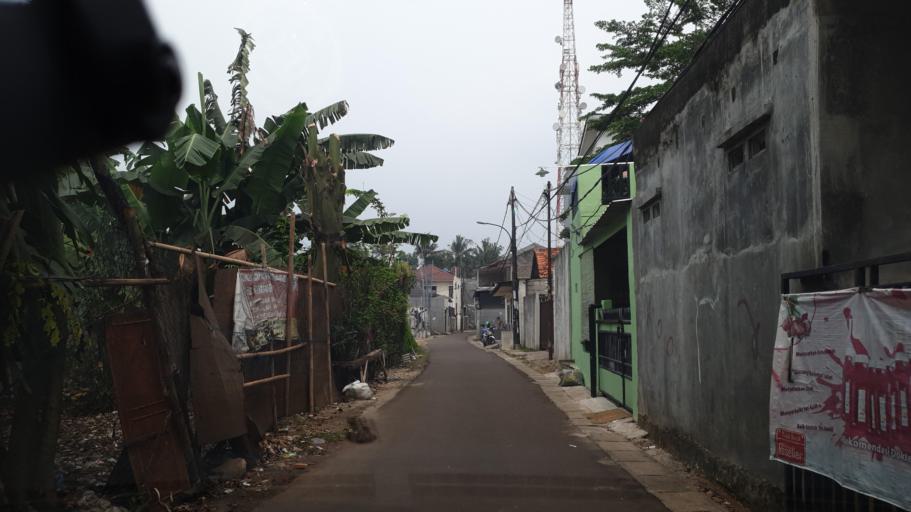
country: ID
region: West Java
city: Pamulang
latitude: -6.3314
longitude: 106.7726
